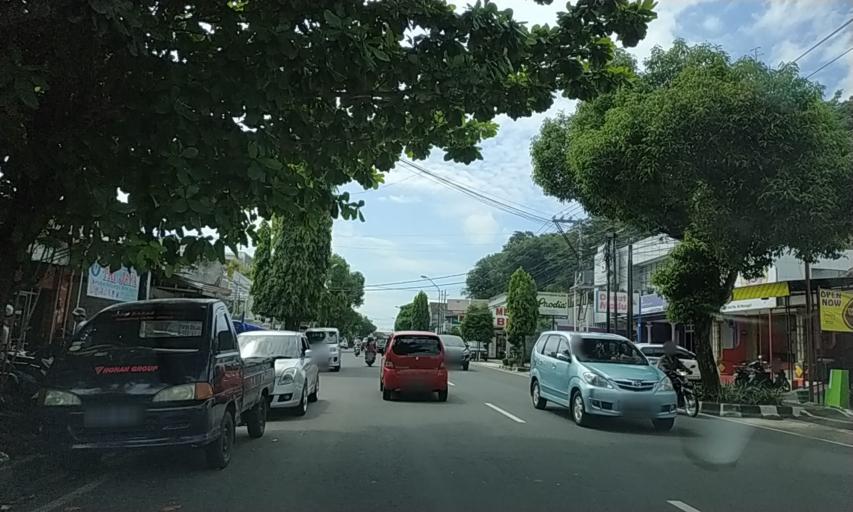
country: ID
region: Central Java
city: Selogiri
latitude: -7.8046
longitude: 110.9174
